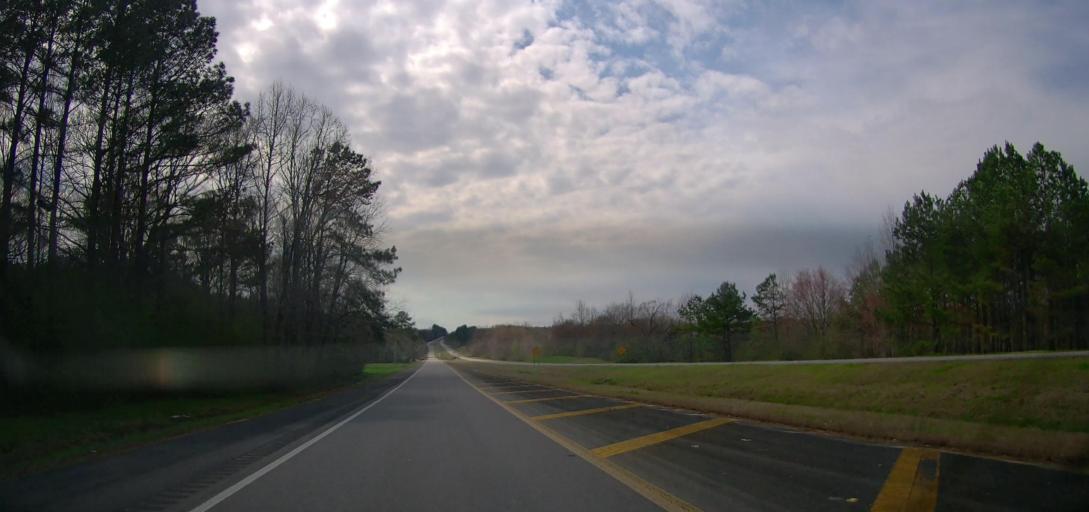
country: US
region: Alabama
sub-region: Marion County
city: Winfield
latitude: 33.9294
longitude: -87.6748
